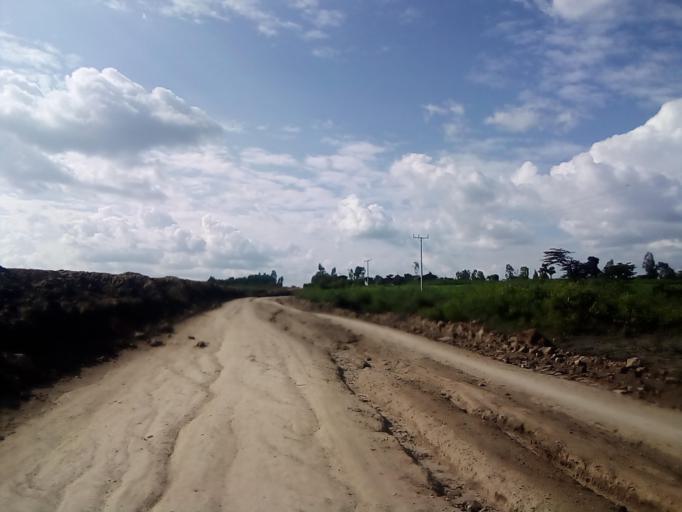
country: ET
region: Southern Nations, Nationalities, and People's Region
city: K'olito
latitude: 7.6297
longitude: 38.0634
